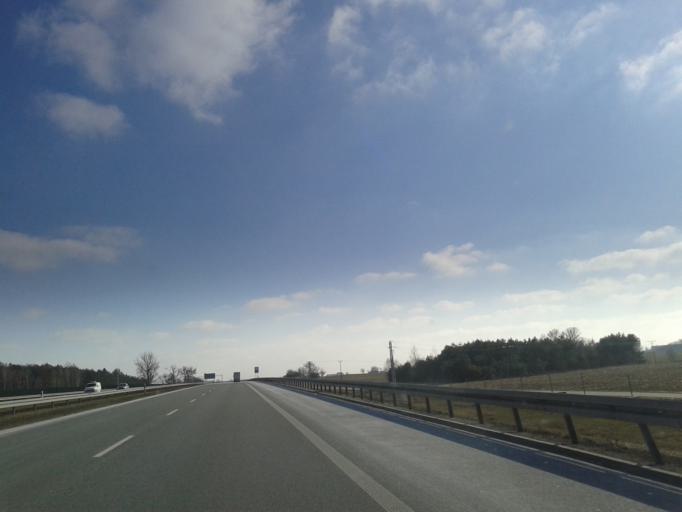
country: PL
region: Kujawsko-Pomorskie
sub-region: Powiat aleksandrowski
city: Ciechocinek
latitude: 52.8549
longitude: 18.7751
